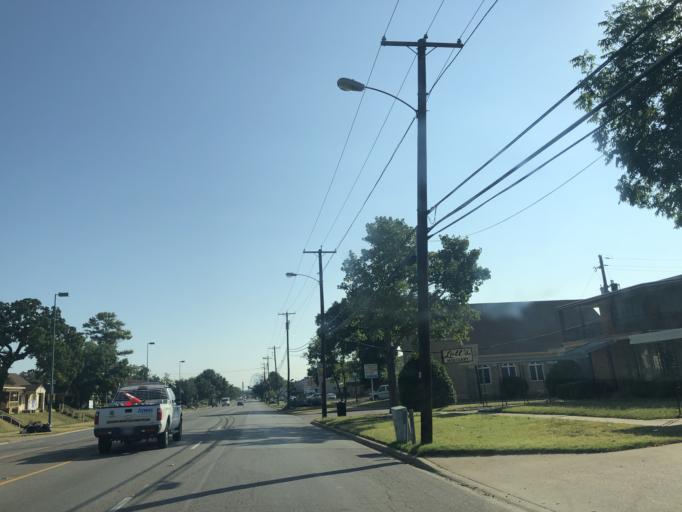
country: US
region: Texas
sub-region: Dallas County
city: Dallas
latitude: 32.7657
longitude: -96.7724
